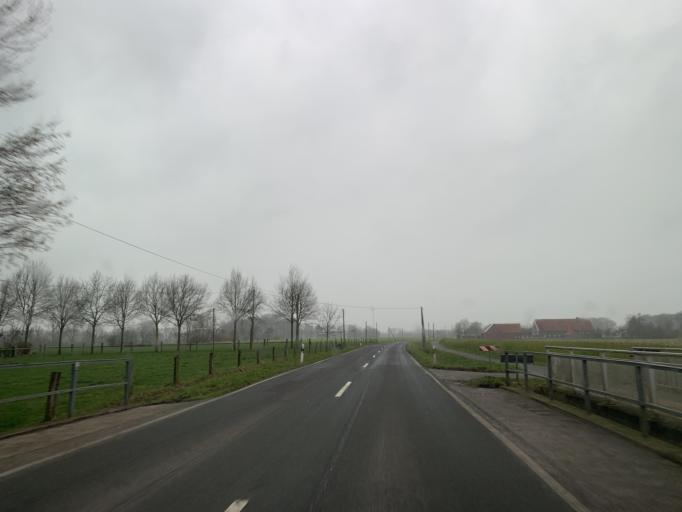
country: DE
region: North Rhine-Westphalia
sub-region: Regierungsbezirk Munster
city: Senden
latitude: 51.8610
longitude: 7.4194
